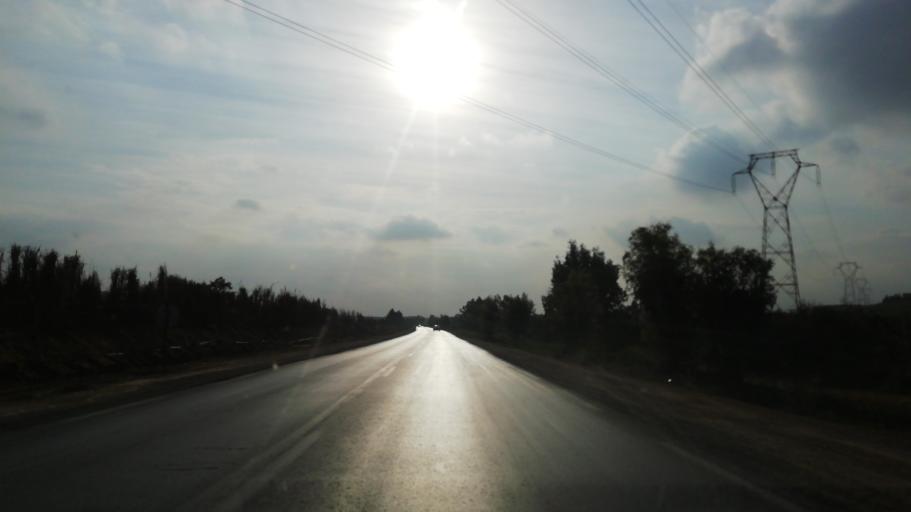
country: DZ
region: Mostaganem
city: Mostaganem
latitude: 35.8450
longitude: 0.0686
